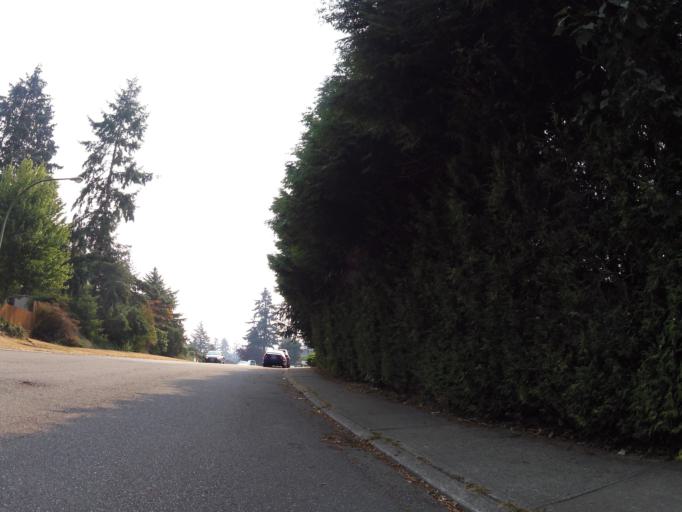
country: CA
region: British Columbia
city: Delta
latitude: 49.1500
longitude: -122.9275
